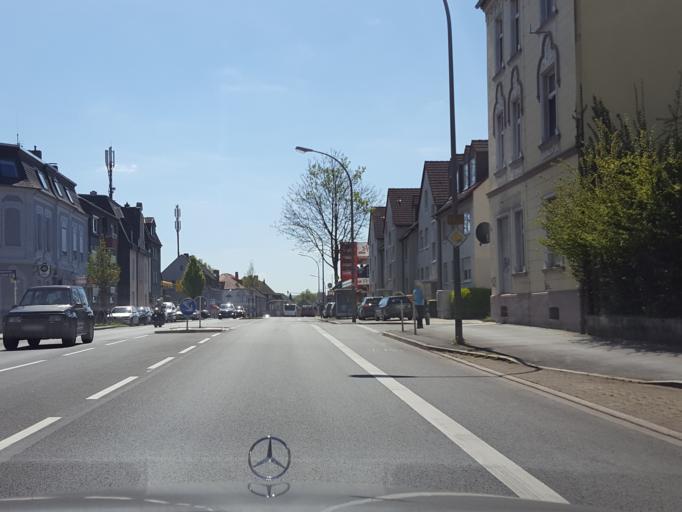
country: DE
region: North Rhine-Westphalia
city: Castrop-Rauxel
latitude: 51.5086
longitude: 7.3234
